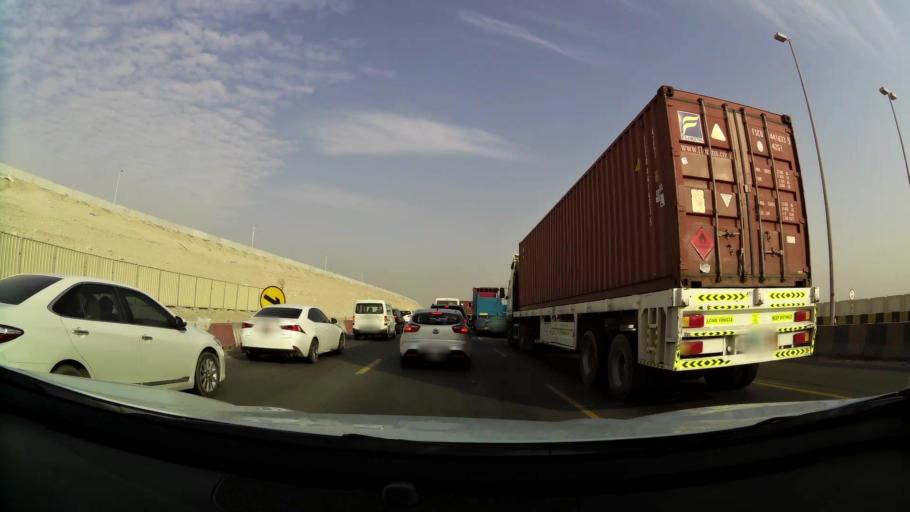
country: AE
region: Abu Dhabi
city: Abu Dhabi
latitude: 24.2841
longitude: 54.5504
